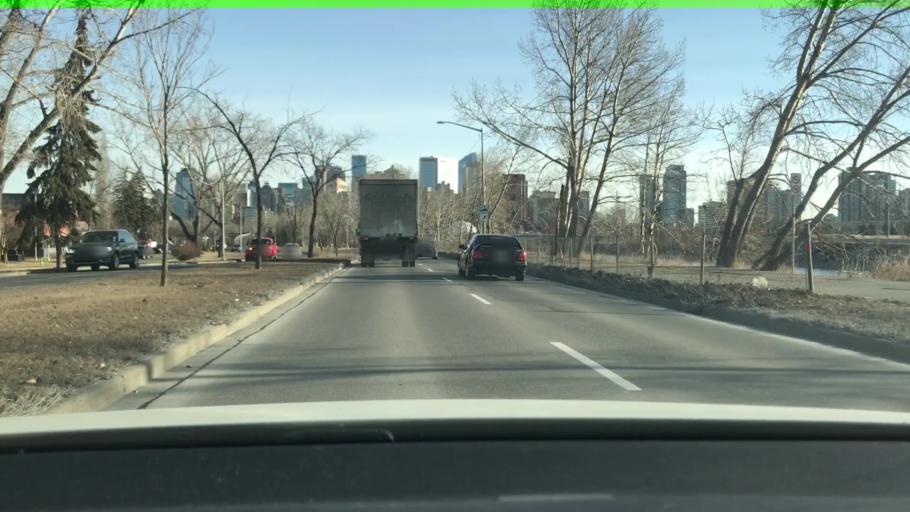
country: CA
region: Alberta
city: Calgary
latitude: 51.0489
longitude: -114.1017
